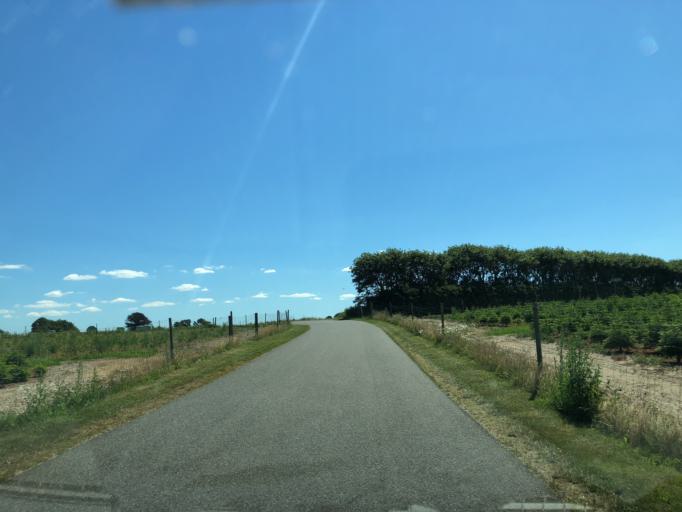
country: DK
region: Central Jutland
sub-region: Viborg Kommune
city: Viborg
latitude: 56.5085
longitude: 9.5184
